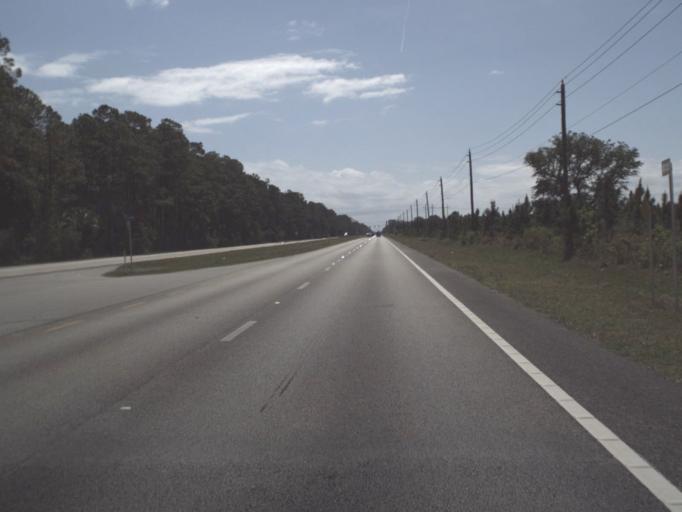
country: US
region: Florida
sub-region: Volusia County
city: Ormond-by-the-Sea
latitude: 29.3593
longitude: -81.1630
